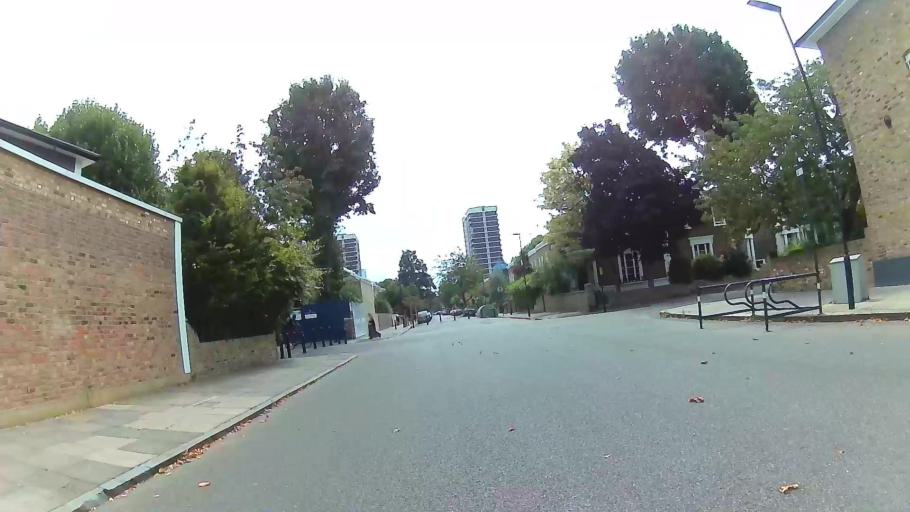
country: GB
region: England
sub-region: Greater London
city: Islington
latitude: 51.5413
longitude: -0.0818
